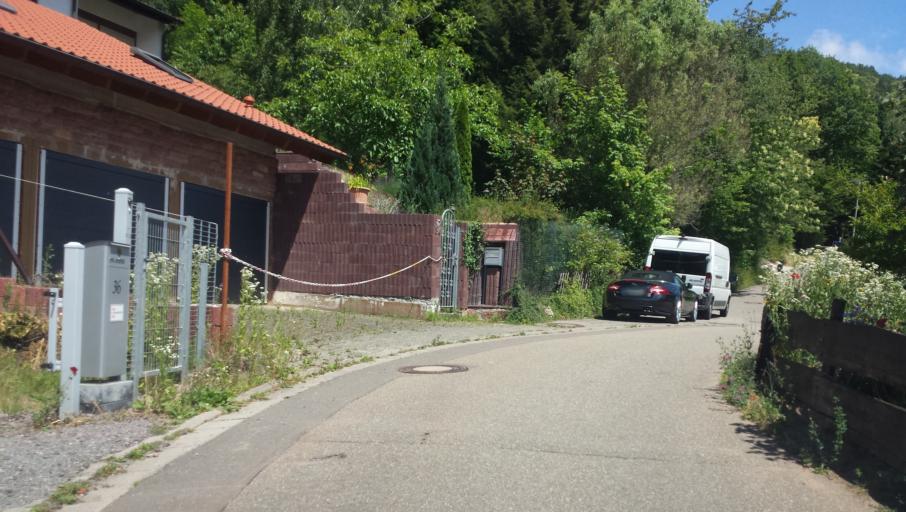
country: DE
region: Rheinland-Pfalz
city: Leinsweiler
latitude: 49.1871
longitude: 8.0084
